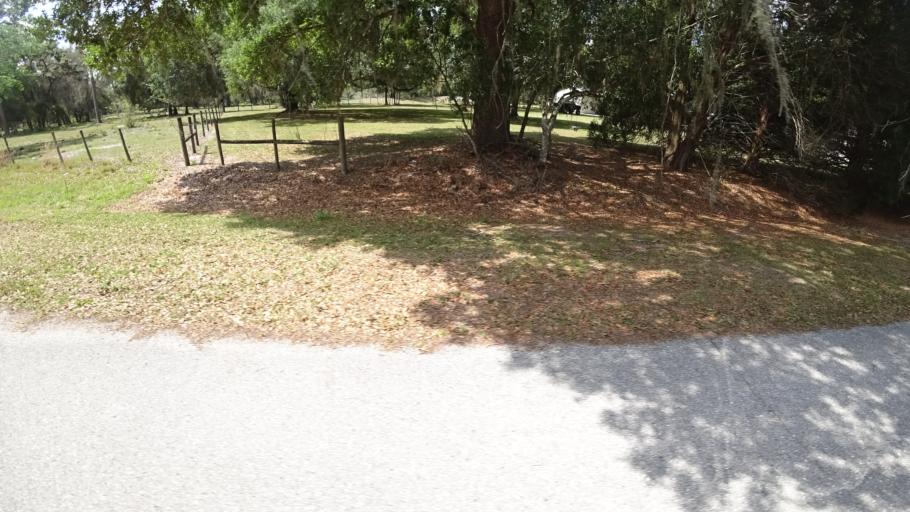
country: US
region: Florida
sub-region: Sarasota County
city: Lake Sarasota
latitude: 27.3498
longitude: -82.1575
